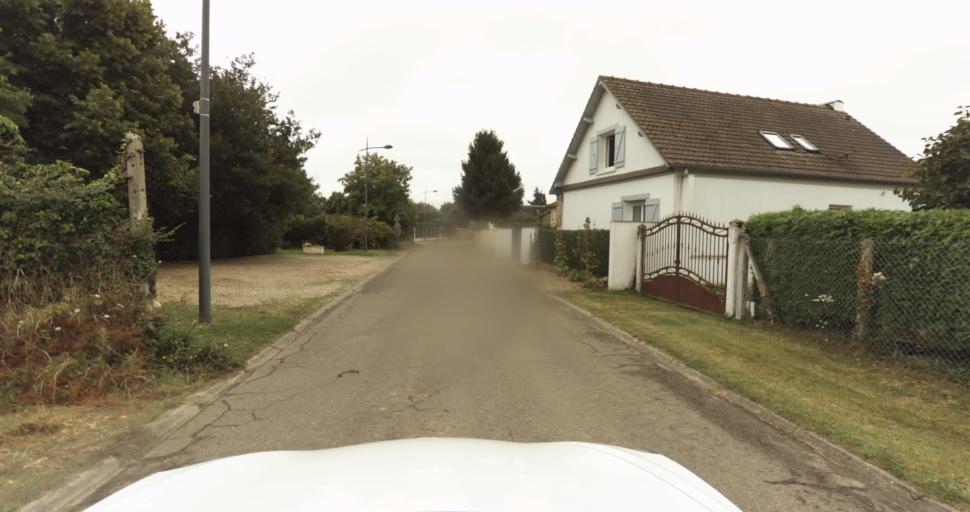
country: FR
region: Haute-Normandie
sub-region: Departement de l'Eure
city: Aviron
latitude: 49.0677
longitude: 1.0713
